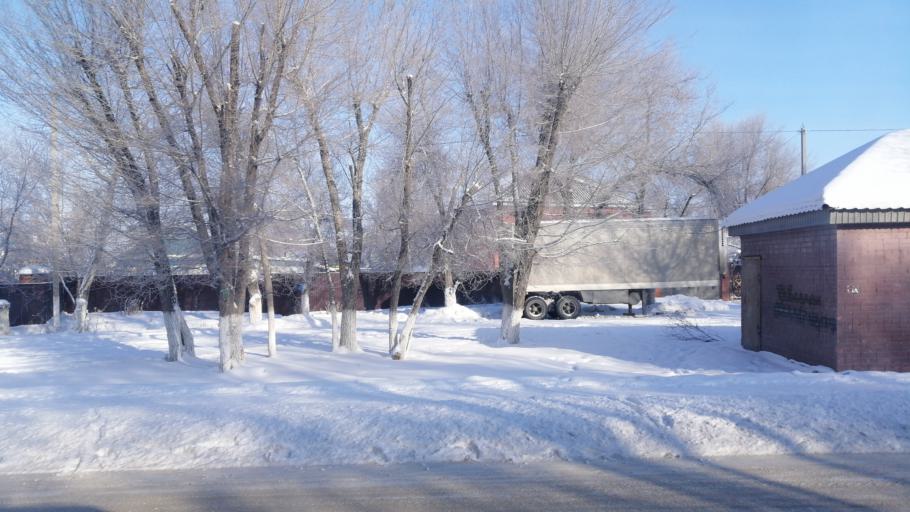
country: KZ
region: Aqtoebe
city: Aqtobe
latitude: 50.2864
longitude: 57.2106
